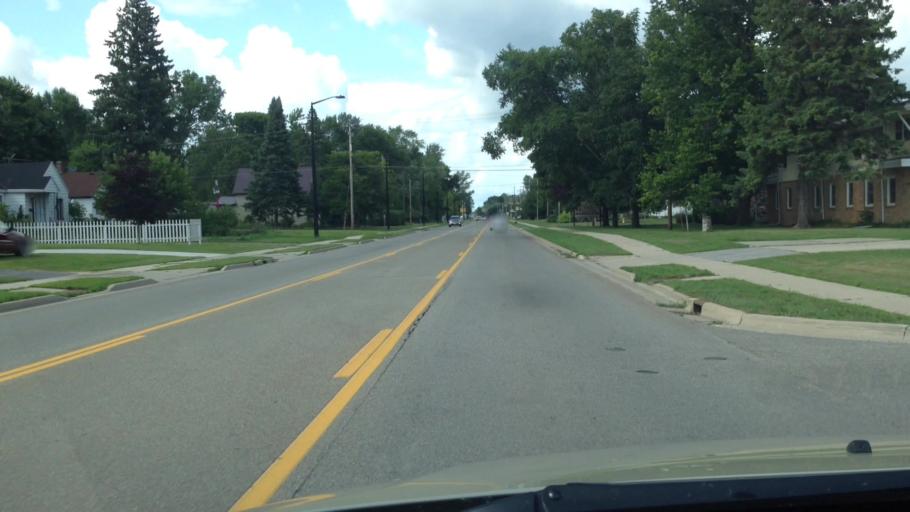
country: US
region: Michigan
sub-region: Menominee County
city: Menominee
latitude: 45.1395
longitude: -87.6122
